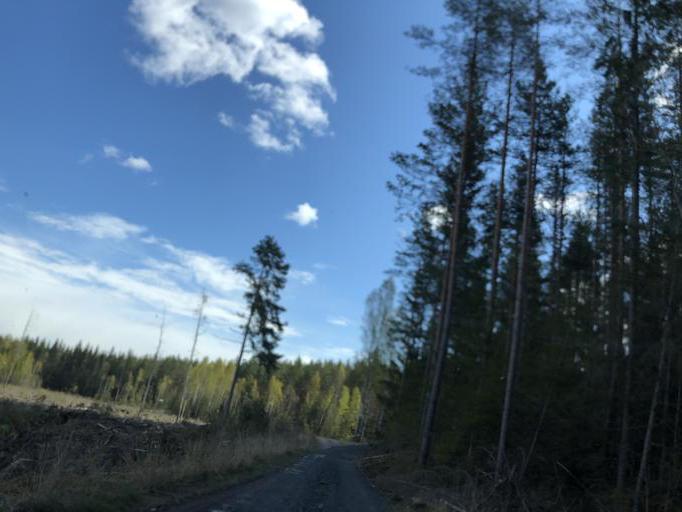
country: SE
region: Uppsala
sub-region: Heby Kommun
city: Tarnsjo
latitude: 60.2321
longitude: 16.7186
